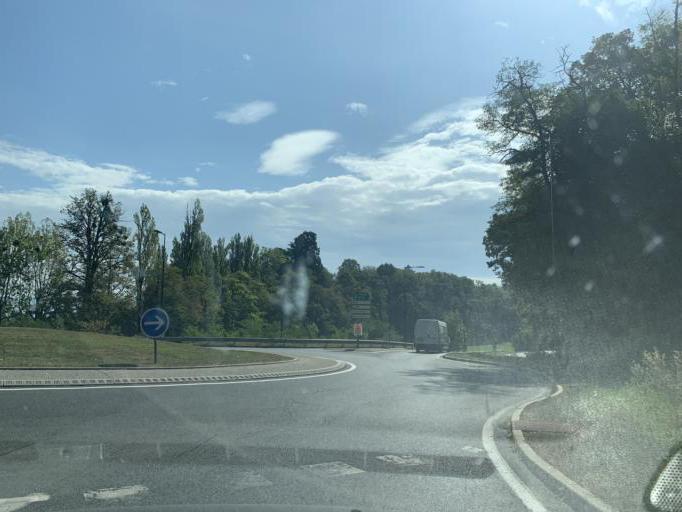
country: FR
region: Rhone-Alpes
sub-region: Departement de l'Ain
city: Divonne-les-Bains
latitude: 46.3585
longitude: 6.1306
